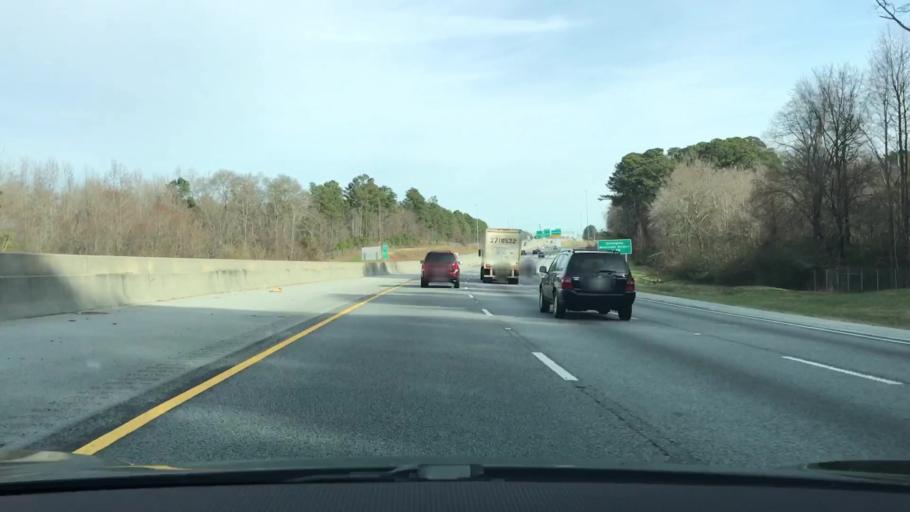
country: US
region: Georgia
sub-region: Newton County
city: Oxford
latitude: 33.6151
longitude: -83.8569
